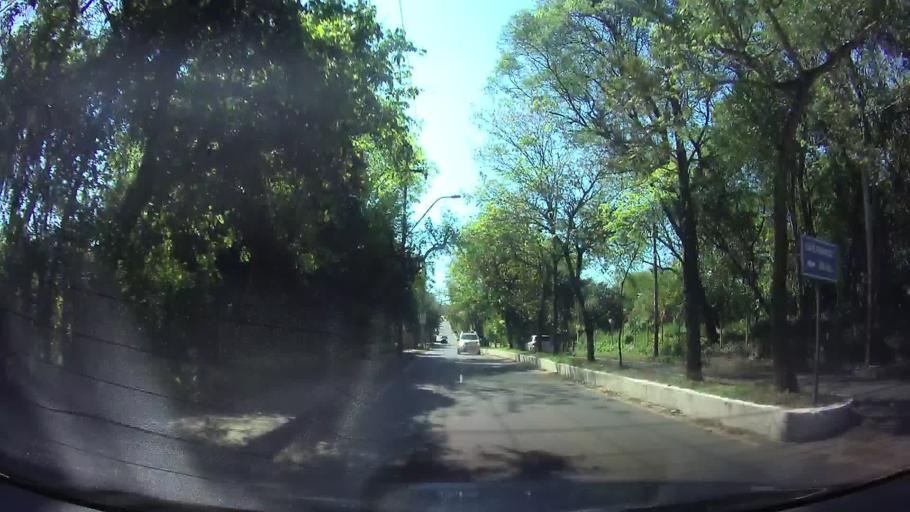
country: PY
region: Cordillera
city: San Bernardino
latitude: -25.3089
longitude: -57.2949
